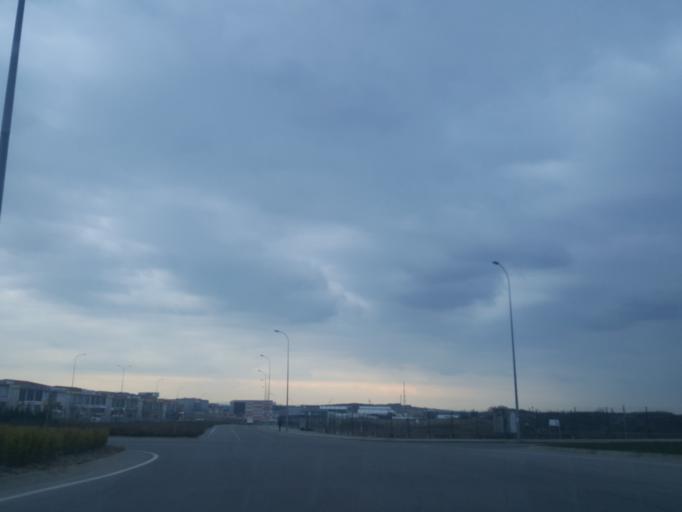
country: TR
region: Kocaeli
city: Tavsanli
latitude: 40.8317
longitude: 29.5708
